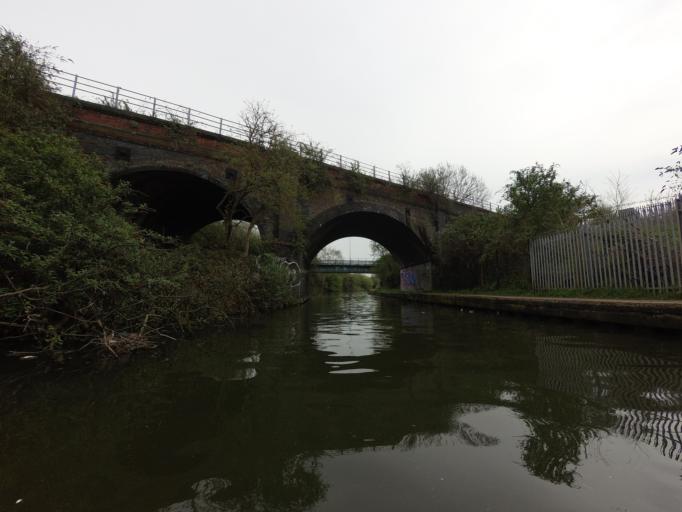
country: GB
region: England
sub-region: Greater London
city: Acton
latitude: 51.5330
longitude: -0.2557
